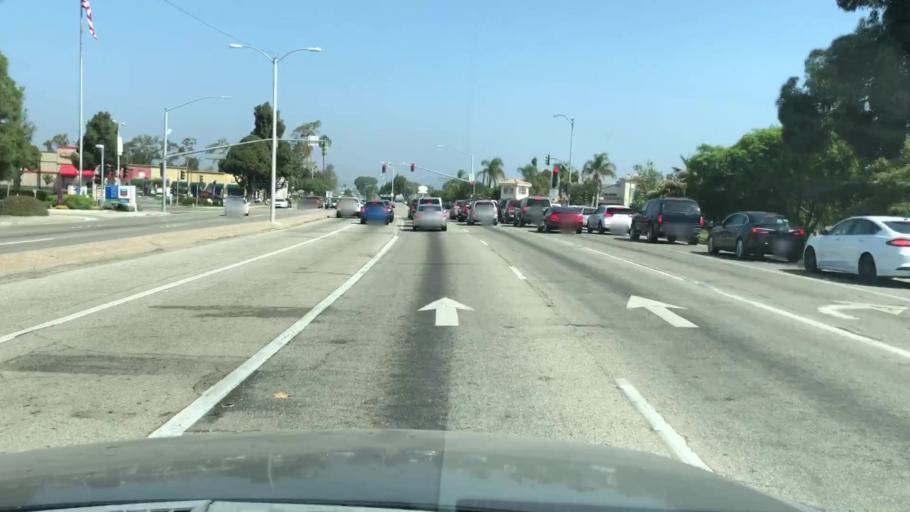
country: US
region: California
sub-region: Ventura County
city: El Rio
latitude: 34.2256
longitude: -119.1771
